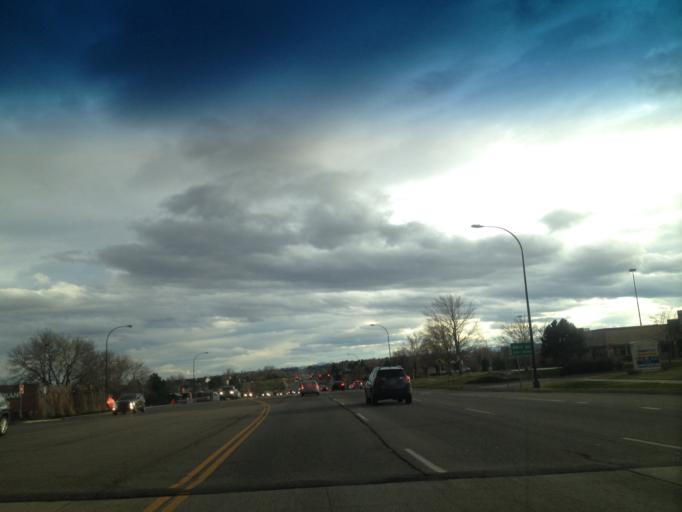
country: US
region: Colorado
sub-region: Adams County
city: Westminster
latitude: 39.8586
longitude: -105.0817
